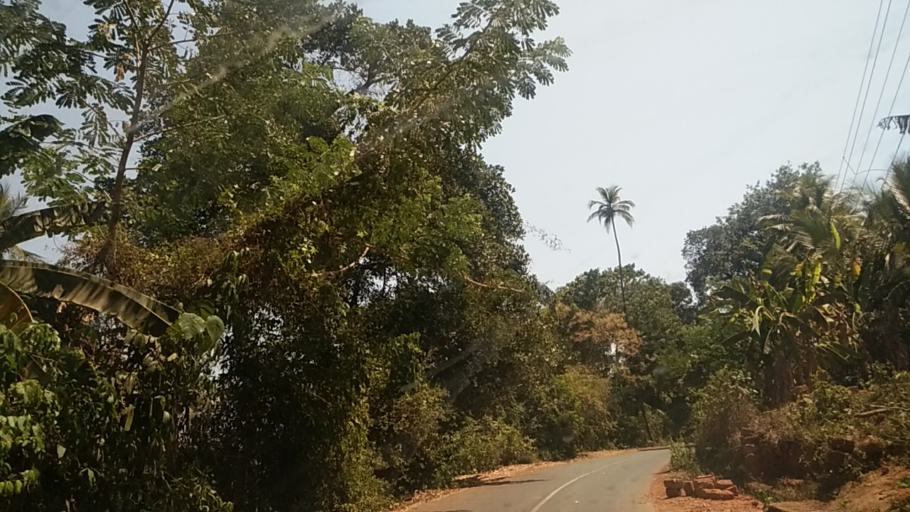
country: IN
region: Goa
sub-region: North Goa
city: Aldona
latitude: 15.5761
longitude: 73.9096
